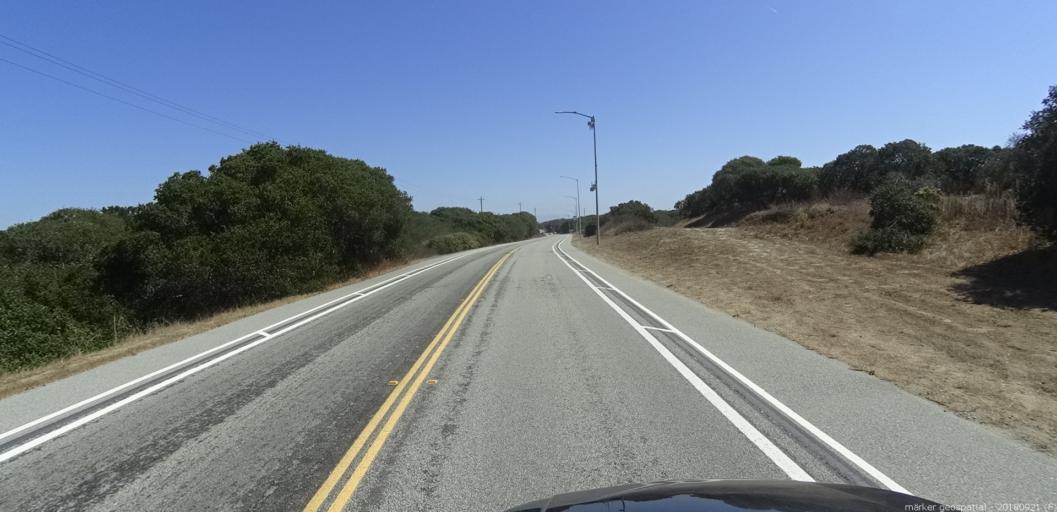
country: US
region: California
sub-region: Monterey County
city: Marina
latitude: 36.6551
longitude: -121.7715
